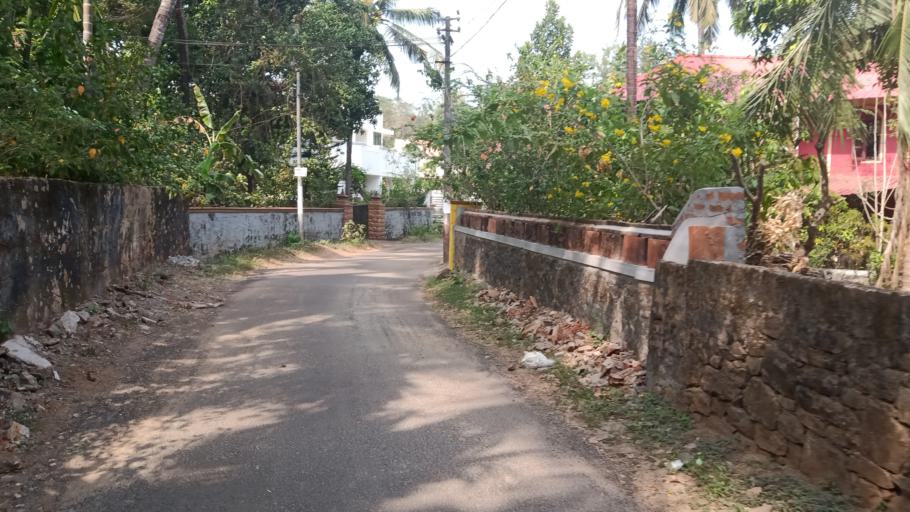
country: IN
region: Kerala
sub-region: Palakkad district
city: Cherpulassery
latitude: 10.8831
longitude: 76.3139
